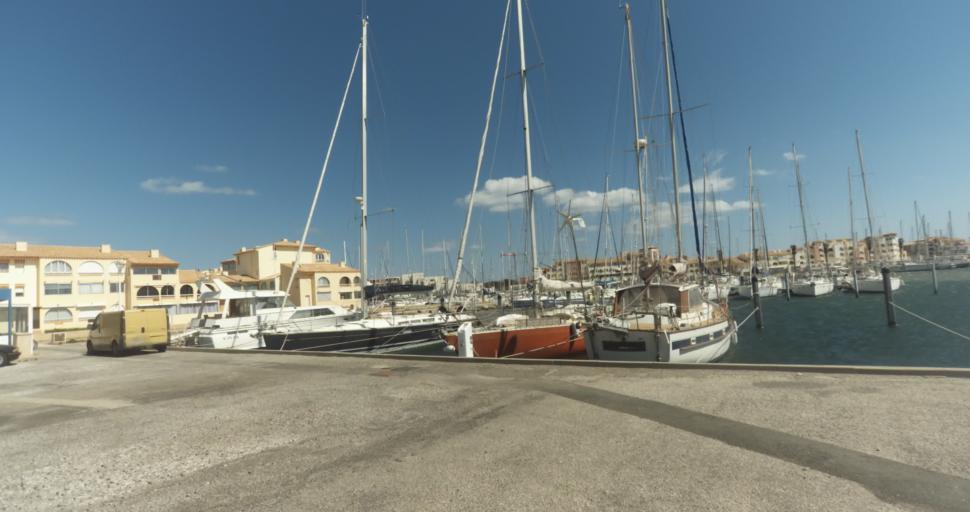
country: FR
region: Languedoc-Roussillon
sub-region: Departement de l'Aude
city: Leucate
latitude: 42.8597
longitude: 3.0349
